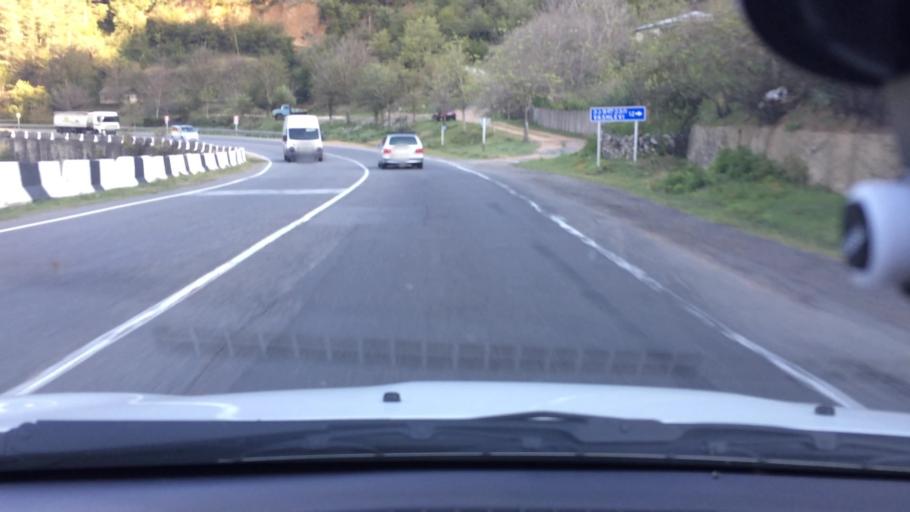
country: GE
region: Imereti
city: Kharagauli
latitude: 42.1075
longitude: 43.3090
